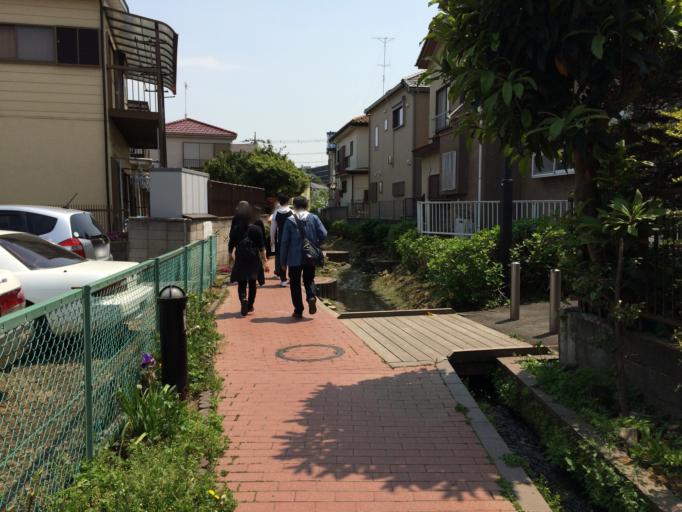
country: JP
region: Kanagawa
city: Yokohama
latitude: 35.5074
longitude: 139.6454
